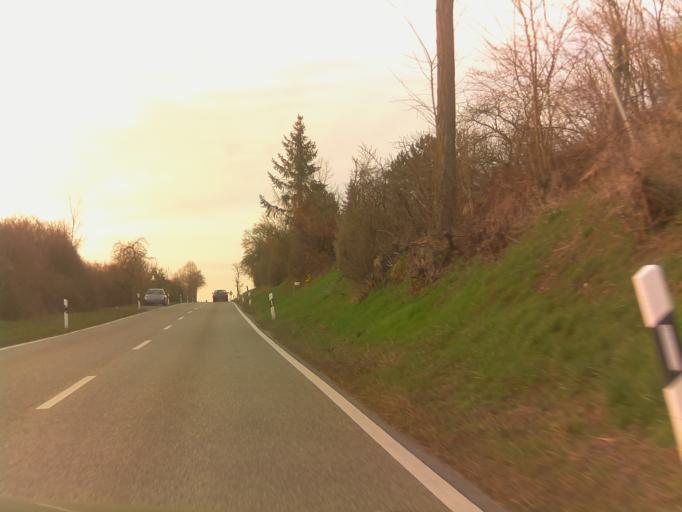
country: DE
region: Baden-Wuerttemberg
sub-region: Regierungsbezirk Stuttgart
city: Hemmingen
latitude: 48.8550
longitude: 9.0301
